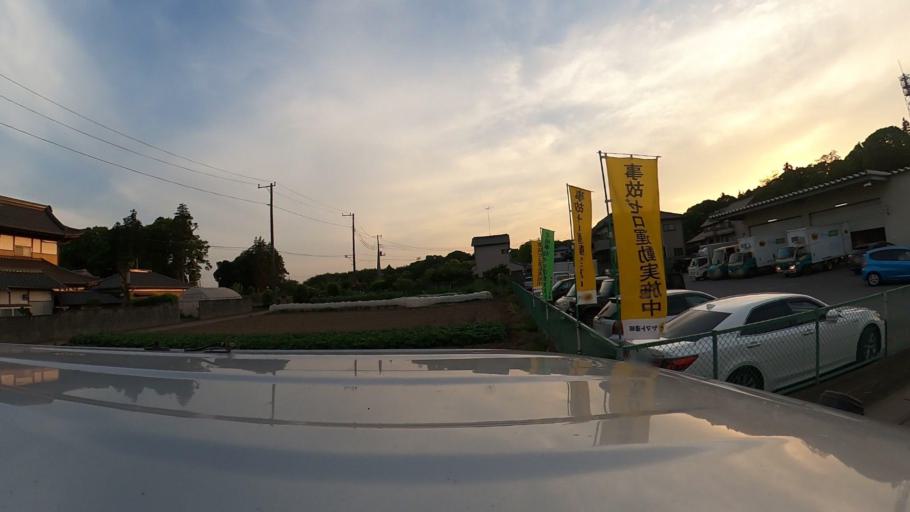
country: JP
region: Ibaraki
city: Ushiku
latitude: 36.0186
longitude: 140.1004
